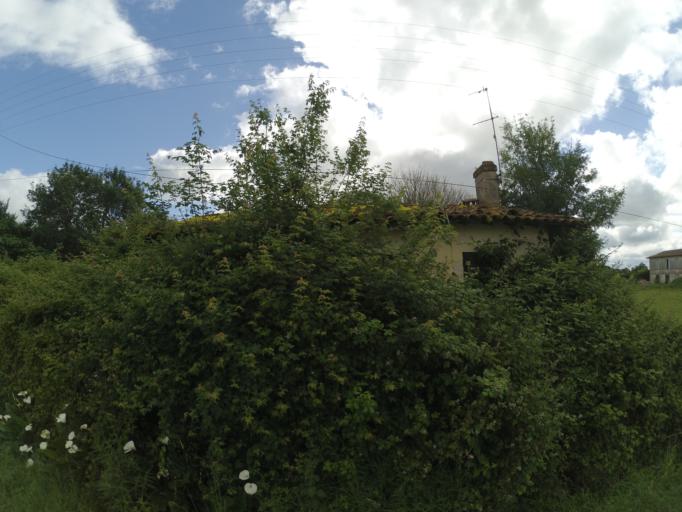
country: FR
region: Aquitaine
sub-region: Departement de la Gironde
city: Ludon-Medoc
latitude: 44.9806
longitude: -0.5638
